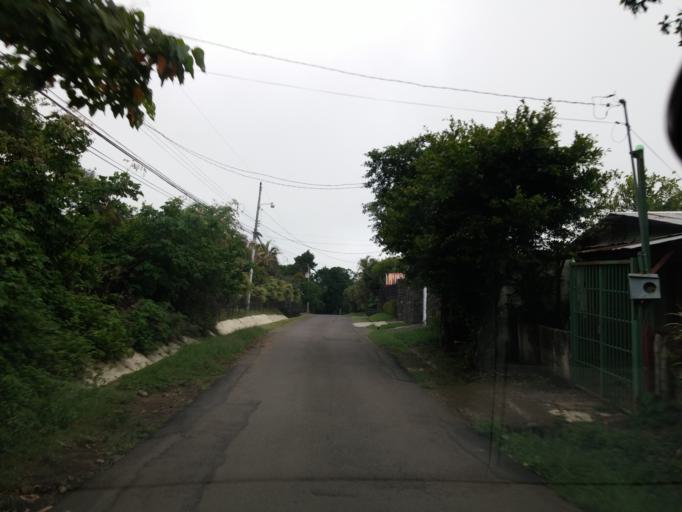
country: CR
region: Heredia
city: San Josecito
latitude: 10.0390
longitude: -84.0988
